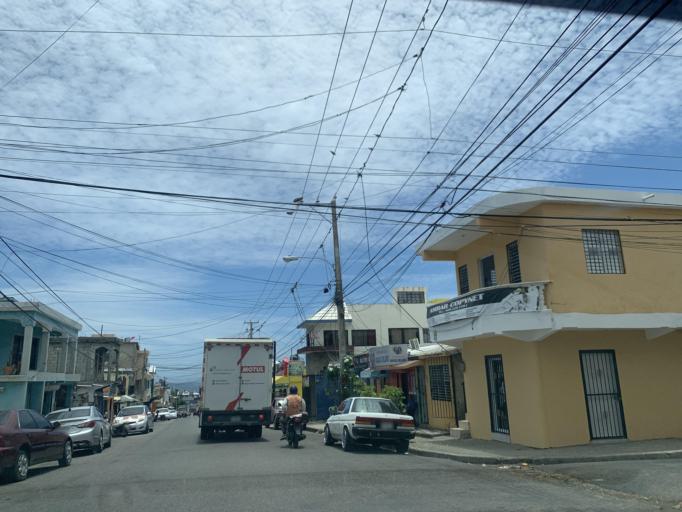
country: DO
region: Puerto Plata
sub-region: Puerto Plata
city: Puerto Plata
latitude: 19.7869
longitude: -70.6874
